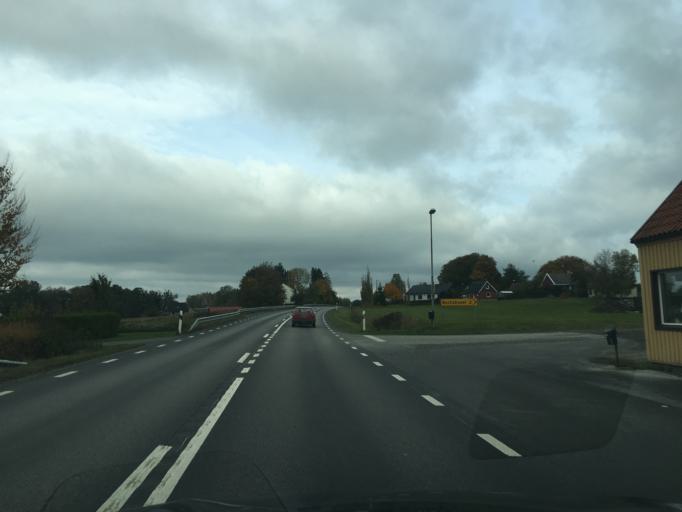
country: SE
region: Skane
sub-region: Tomelilla Kommun
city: Tomelilla
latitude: 55.6442
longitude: 14.0086
